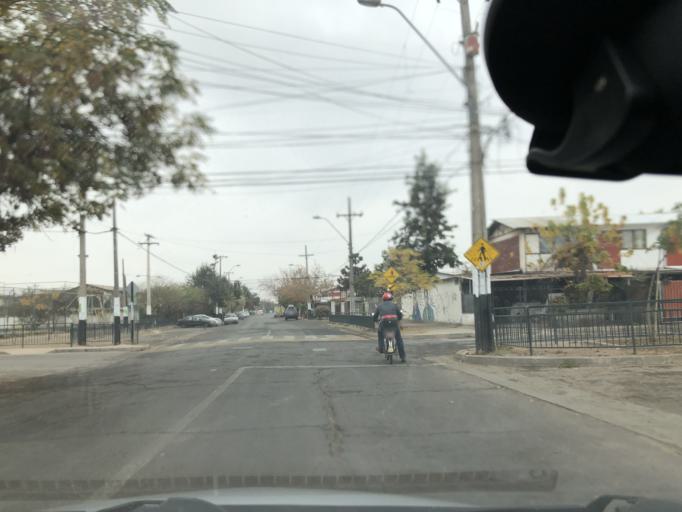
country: CL
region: Santiago Metropolitan
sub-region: Provincia de Cordillera
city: Puente Alto
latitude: -33.5823
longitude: -70.5885
